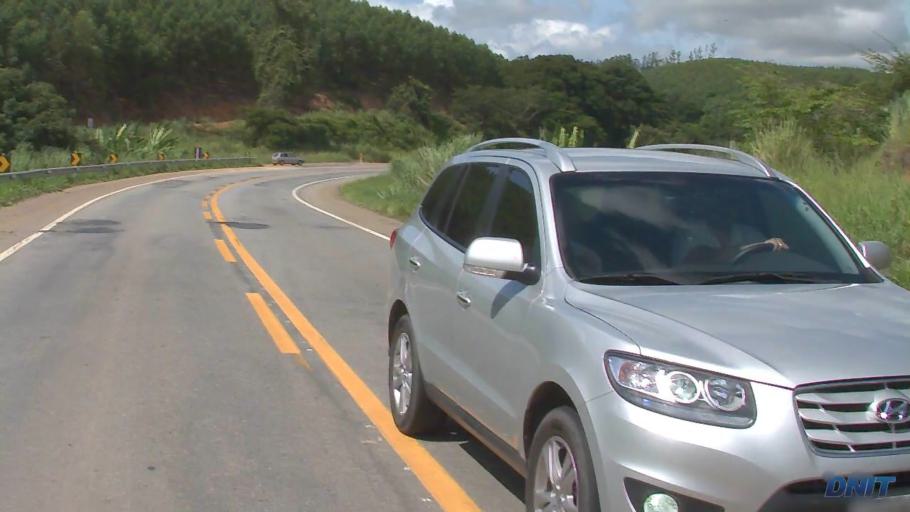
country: BR
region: Minas Gerais
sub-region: Belo Oriente
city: Belo Oriente
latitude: -19.1142
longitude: -42.2067
